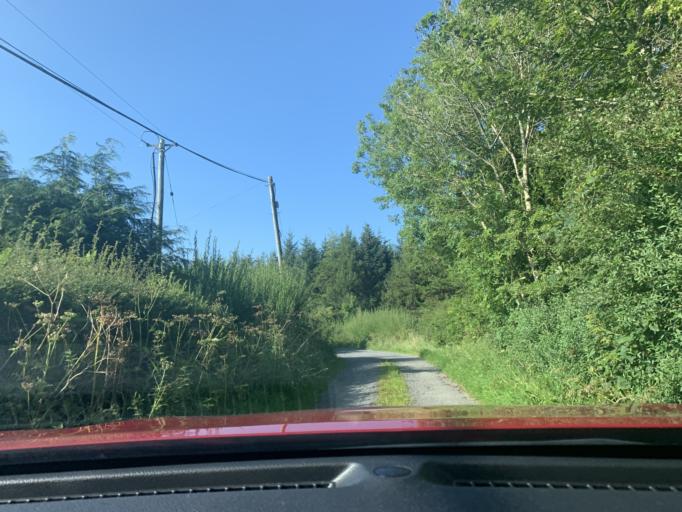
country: IE
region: Connaught
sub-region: Sligo
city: Tobercurry
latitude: 54.0600
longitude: -8.7936
